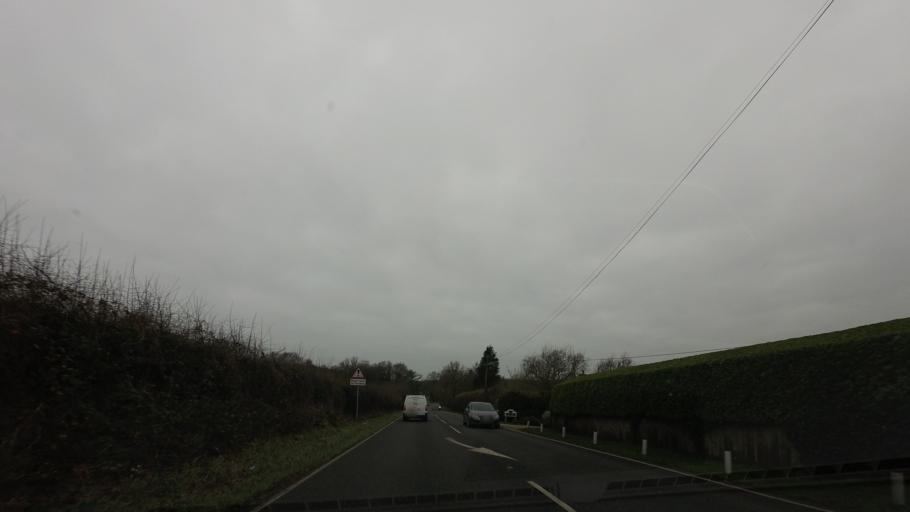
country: GB
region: England
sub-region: East Sussex
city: Battle
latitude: 50.9284
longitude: 0.5284
